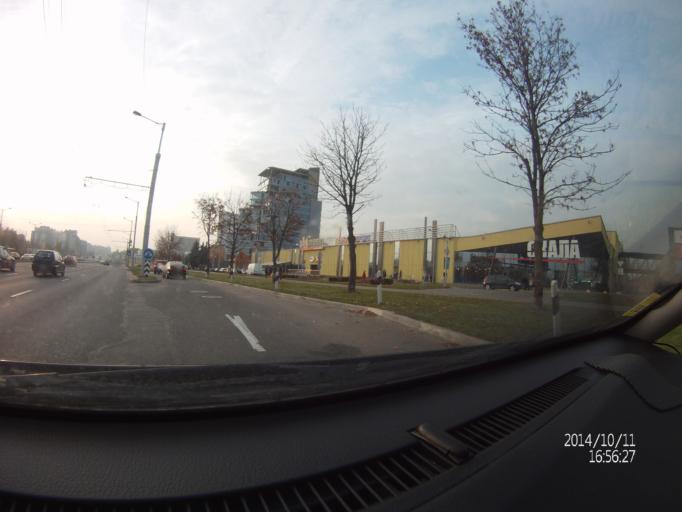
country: BY
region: Minsk
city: Novoye Medvezhino
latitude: 53.9080
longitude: 27.4708
